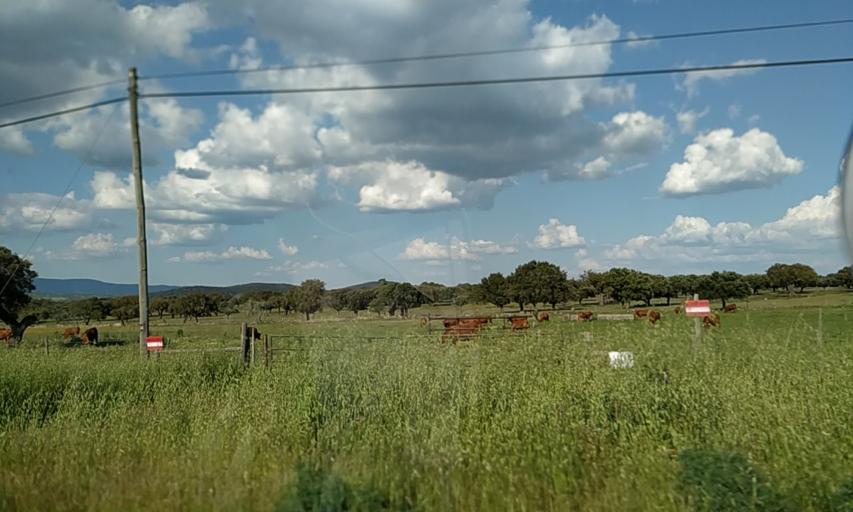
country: PT
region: Portalegre
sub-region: Portalegre
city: Urra
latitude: 39.1826
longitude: -7.4552
